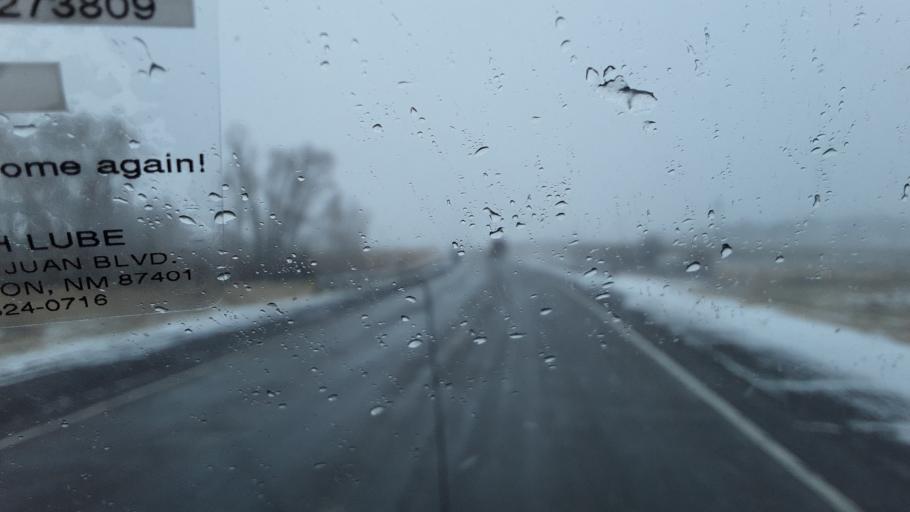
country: US
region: New Mexico
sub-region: Rio Arriba County
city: Chama
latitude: 36.8417
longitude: -106.5697
